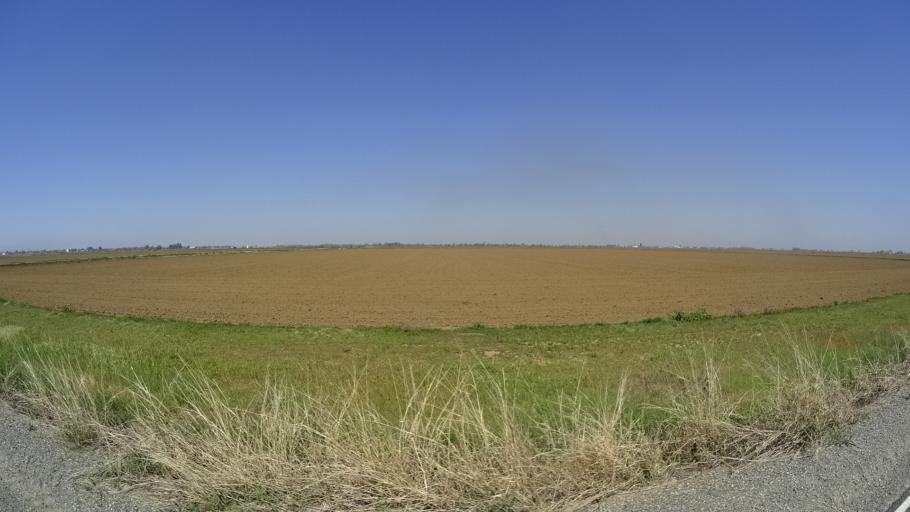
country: US
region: California
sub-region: Glenn County
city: Willows
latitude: 39.4948
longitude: -122.1599
